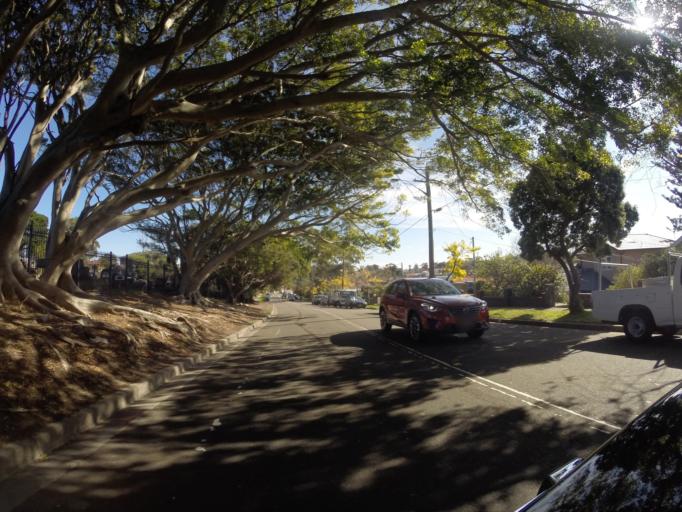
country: AU
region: New South Wales
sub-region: Randwick
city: South Coogee
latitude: -33.9287
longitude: 151.2545
